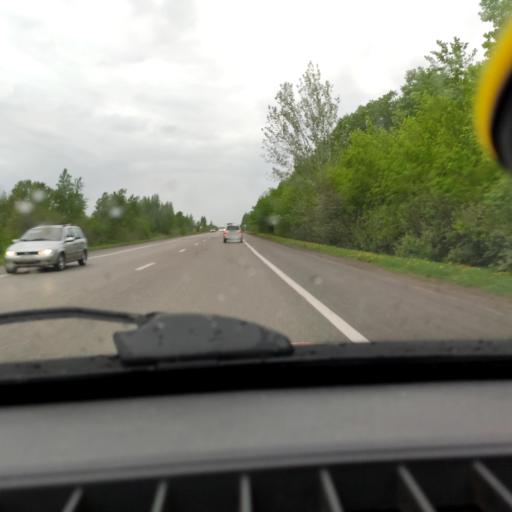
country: RU
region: Samara
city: Tol'yatti
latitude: 53.6967
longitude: 49.4197
